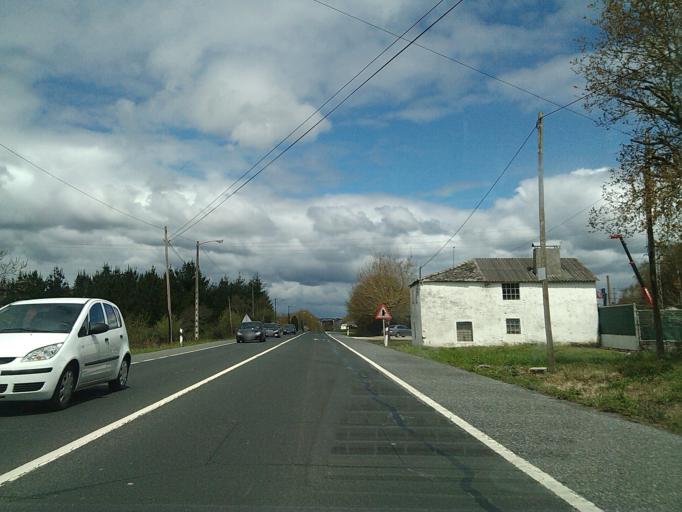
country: ES
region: Galicia
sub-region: Provincia de Lugo
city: Outeiro de Rei
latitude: 43.1082
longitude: -7.6151
